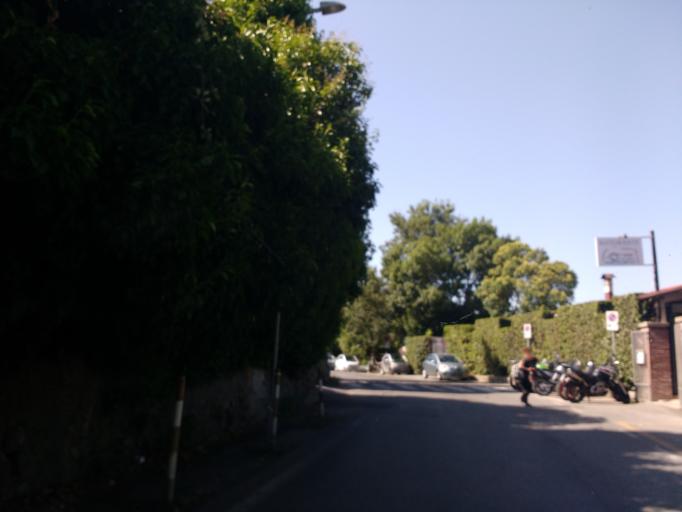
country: IT
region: Latium
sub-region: Citta metropolitana di Roma Capitale
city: Castel Gandolfo
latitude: 41.7491
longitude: 12.6539
